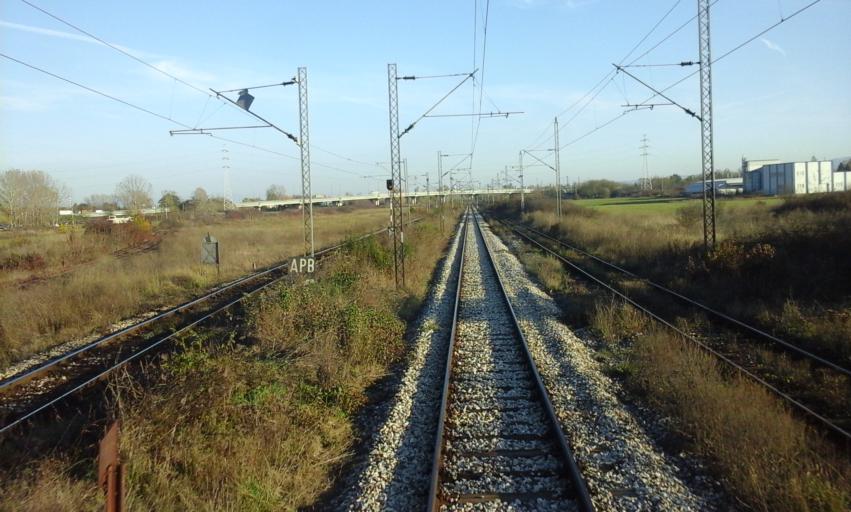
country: RS
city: Veternik
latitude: 45.2818
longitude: 19.7951
